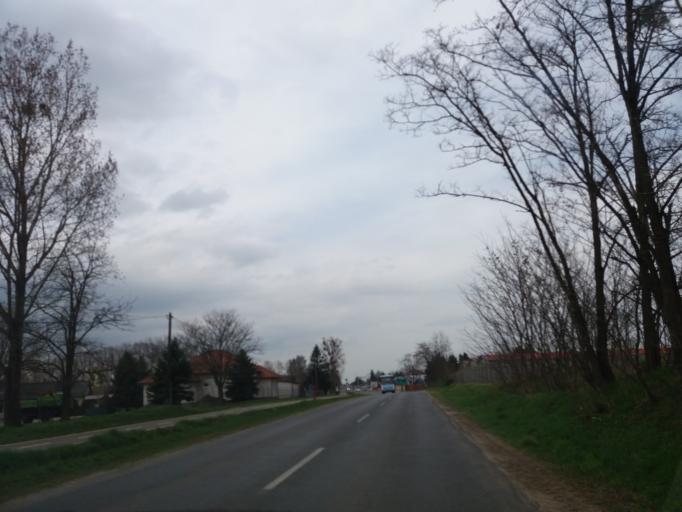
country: HU
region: Szabolcs-Szatmar-Bereg
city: Kisvarda
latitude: 48.1975
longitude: 22.0955
